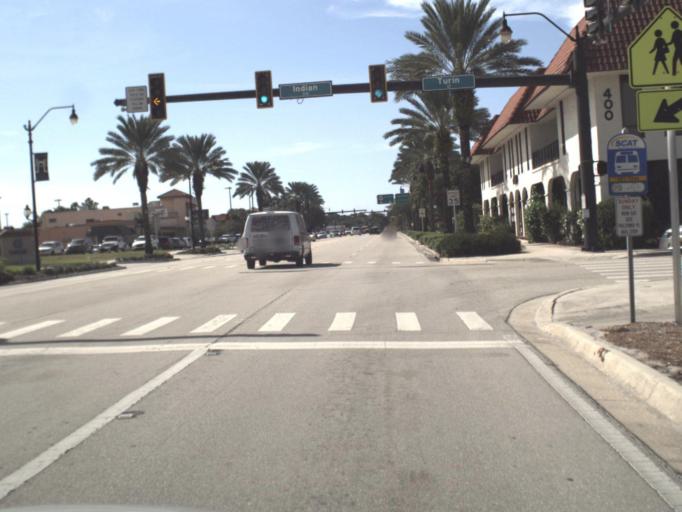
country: US
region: Florida
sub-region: Sarasota County
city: Venice
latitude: 27.0944
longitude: -82.4444
